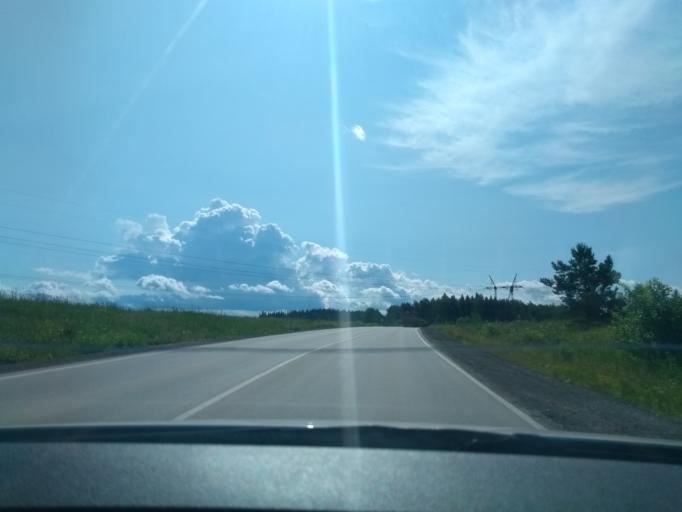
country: RU
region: Perm
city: Lobanovo
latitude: 57.8379
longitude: 56.3941
